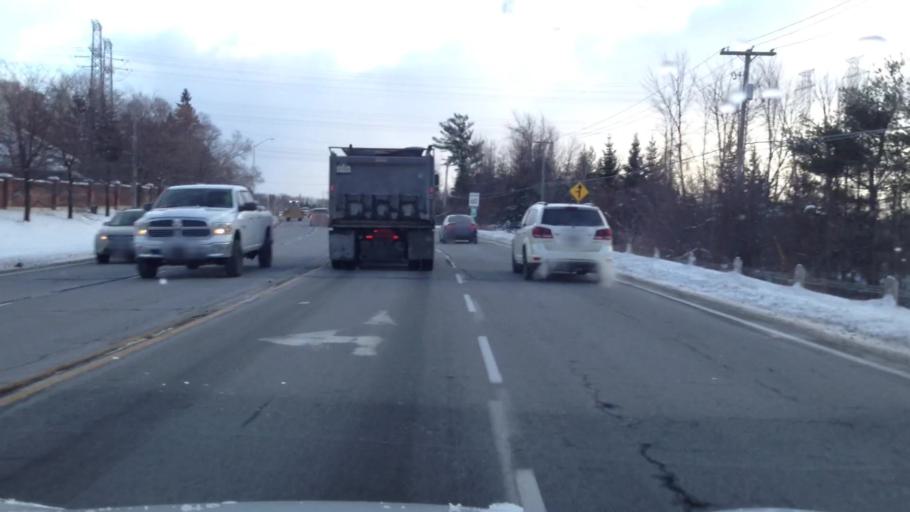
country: CA
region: Ontario
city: Ottawa
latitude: 45.3511
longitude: -75.7039
